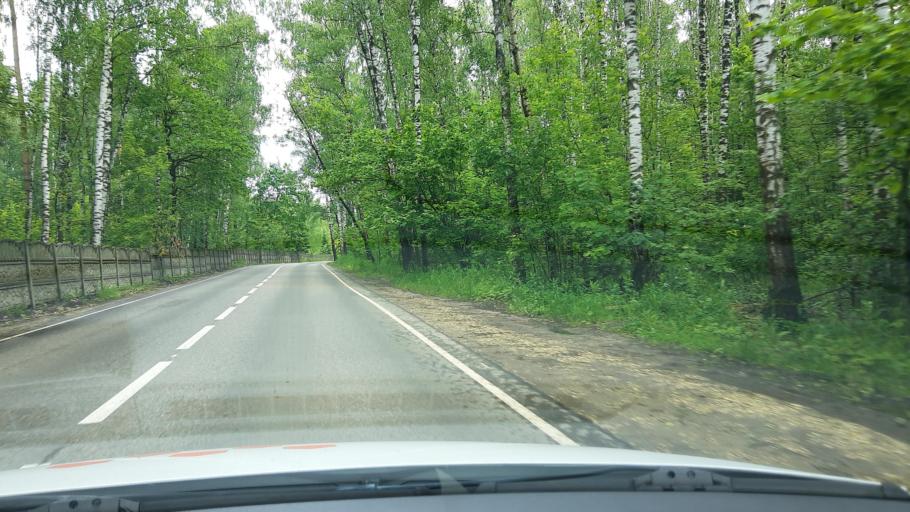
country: RU
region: Moskovskaya
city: Elektrostal'
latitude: 55.7687
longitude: 38.4059
